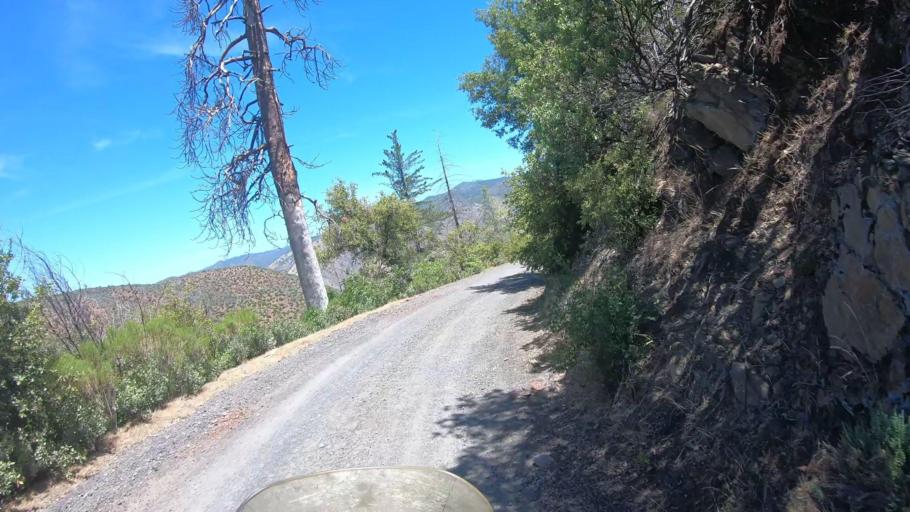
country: US
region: California
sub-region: Tuolumne County
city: Tuolumne City
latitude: 37.8327
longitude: -120.1137
